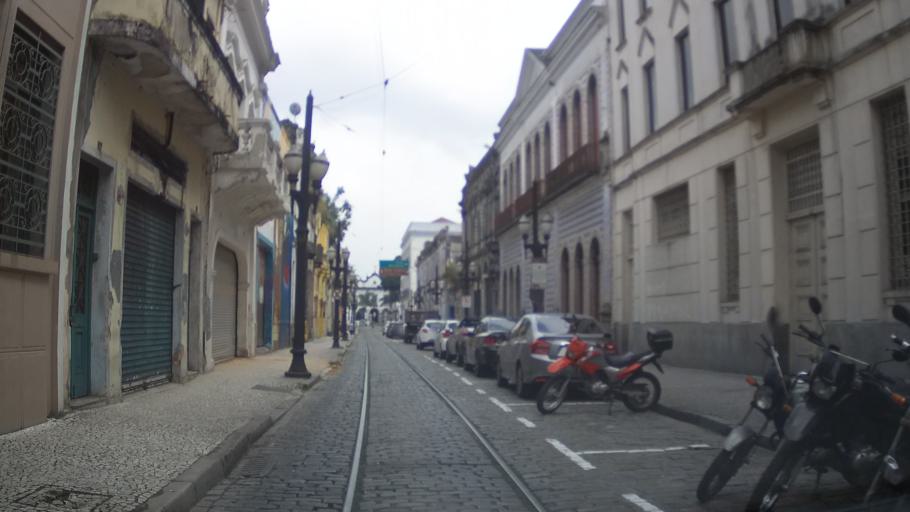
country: BR
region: Sao Paulo
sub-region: Santos
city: Santos
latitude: -23.9324
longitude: -46.3321
